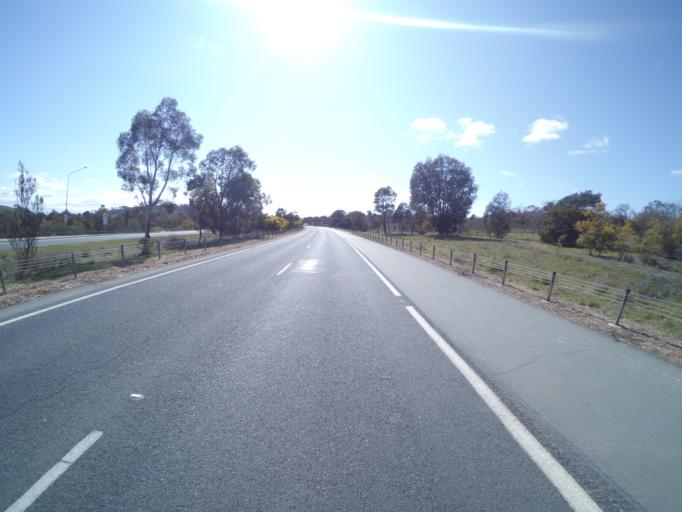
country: AU
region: Australian Capital Territory
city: Kaleen
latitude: -35.2202
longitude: 149.1787
